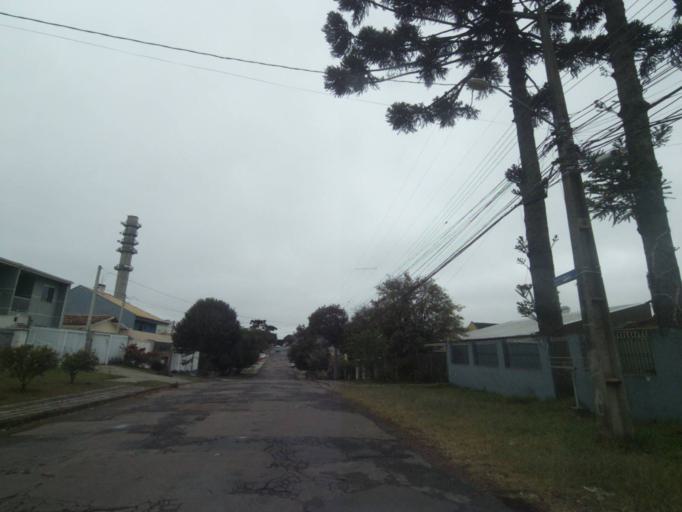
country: BR
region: Parana
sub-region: Curitiba
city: Curitiba
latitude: -25.5016
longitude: -49.3064
